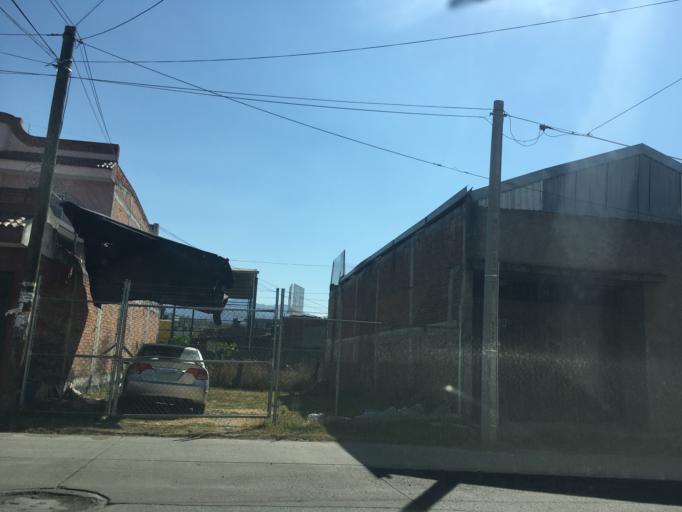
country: MX
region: Michoacan
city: Morelia
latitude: 19.6734
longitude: -101.2092
